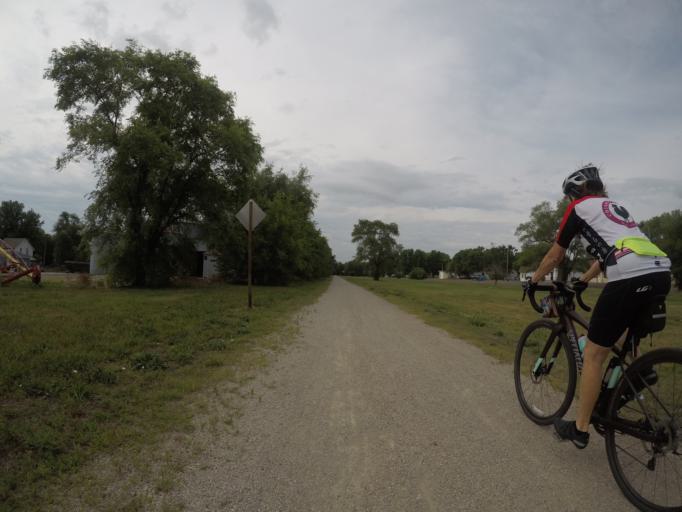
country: US
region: Kansas
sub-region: Franklin County
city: Ottawa
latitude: 38.4890
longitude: -95.2743
